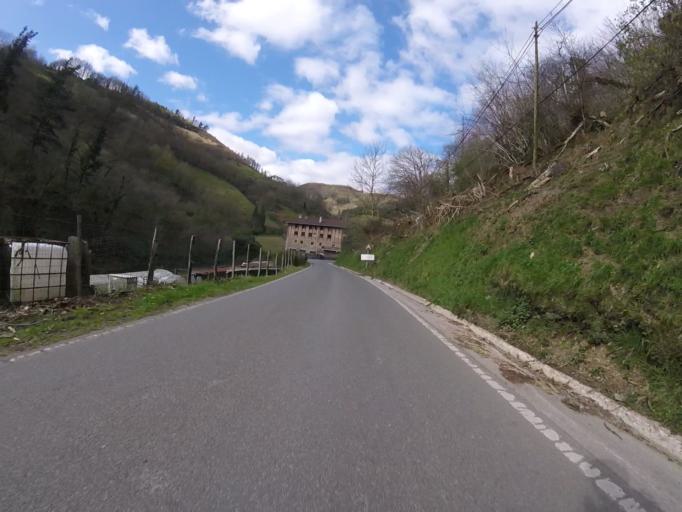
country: ES
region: Navarre
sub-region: Provincia de Navarra
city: Goizueta
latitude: 43.1691
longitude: -1.8607
